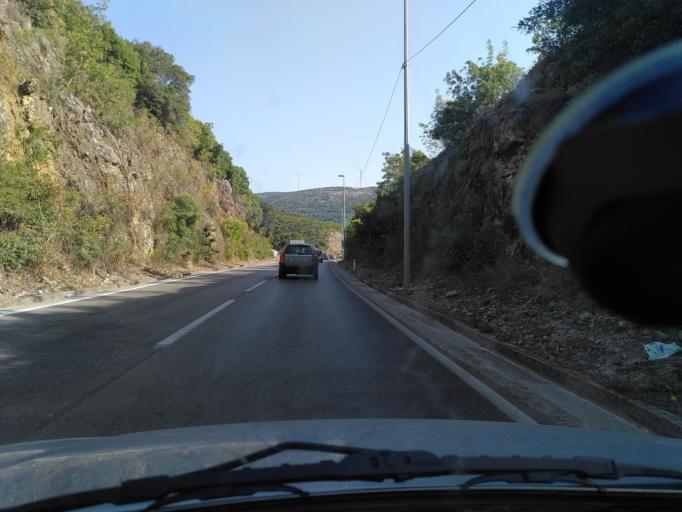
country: ME
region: Ulcinj
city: Ulcinj
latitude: 41.9576
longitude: 19.1908
